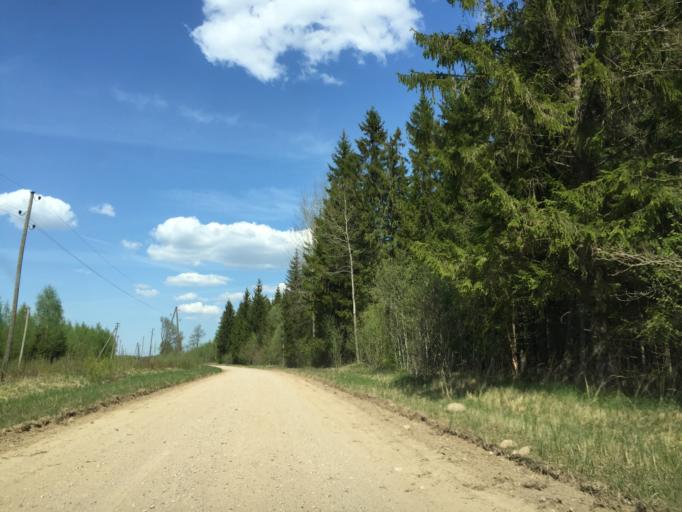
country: LV
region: Limbazu Rajons
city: Limbazi
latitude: 57.3670
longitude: 24.6360
